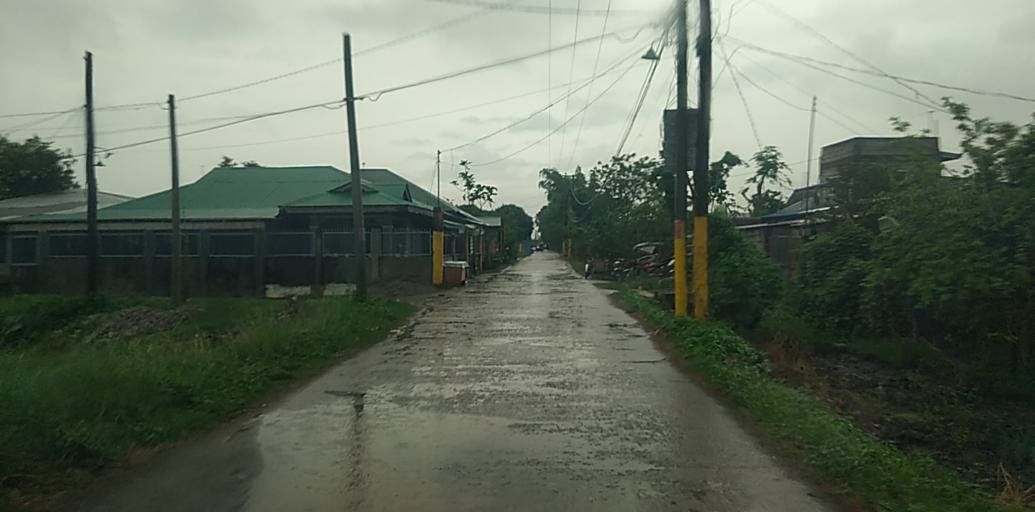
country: PH
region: Central Luzon
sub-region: Province of Pampanga
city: Panlinlang
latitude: 15.1575
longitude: 120.7222
